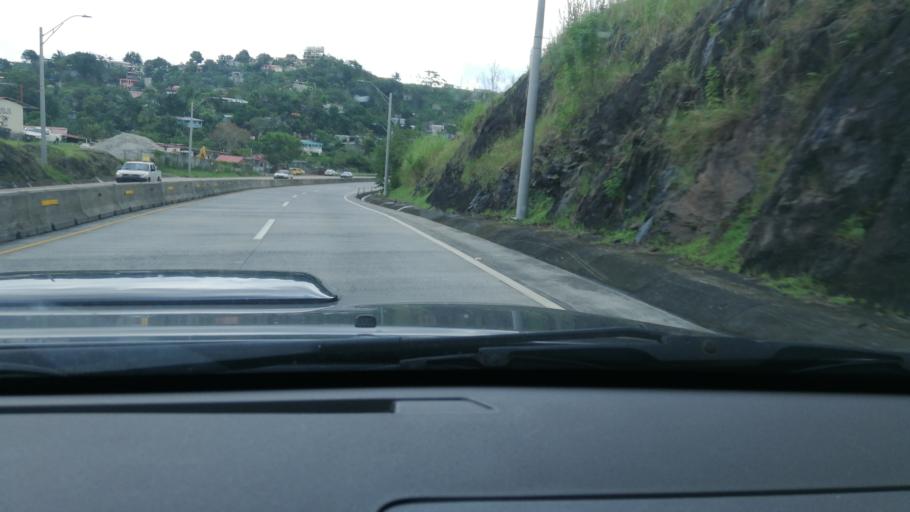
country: PA
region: Panama
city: San Miguelito
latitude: 9.0583
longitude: -79.4811
